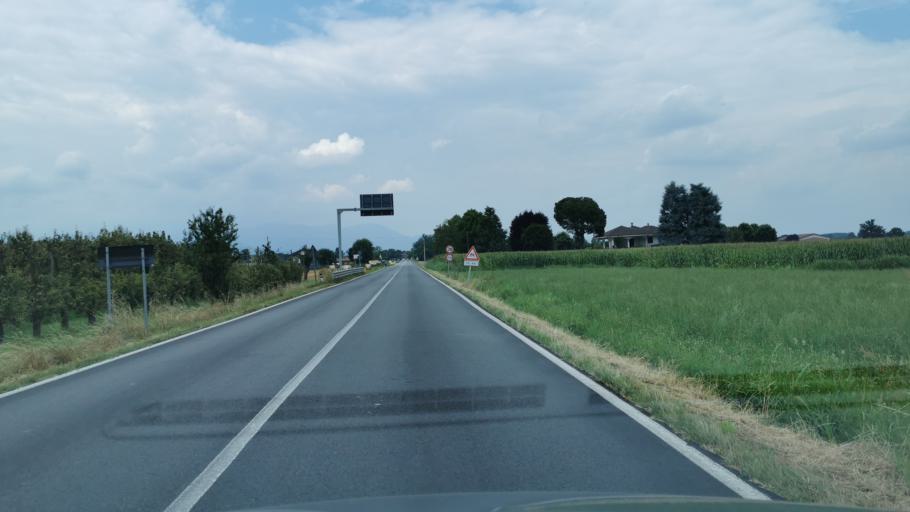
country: IT
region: Piedmont
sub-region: Provincia di Torino
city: Garzigliana
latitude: 44.8177
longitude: 7.3711
